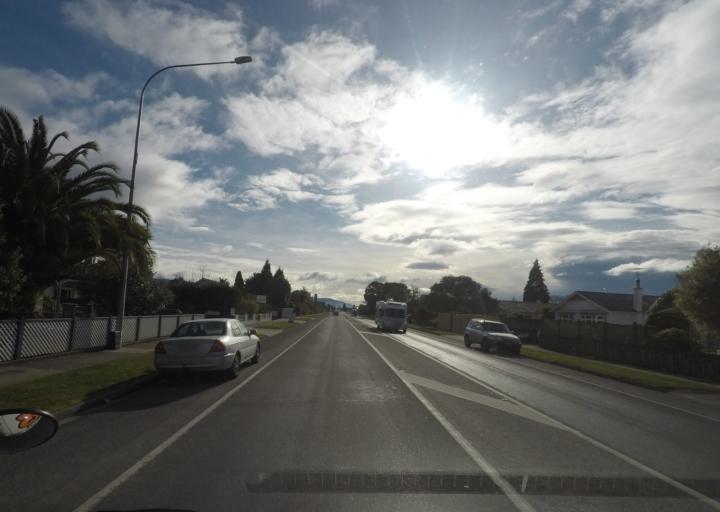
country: NZ
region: Tasman
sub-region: Tasman District
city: Motueka
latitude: -41.1265
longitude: 173.0104
